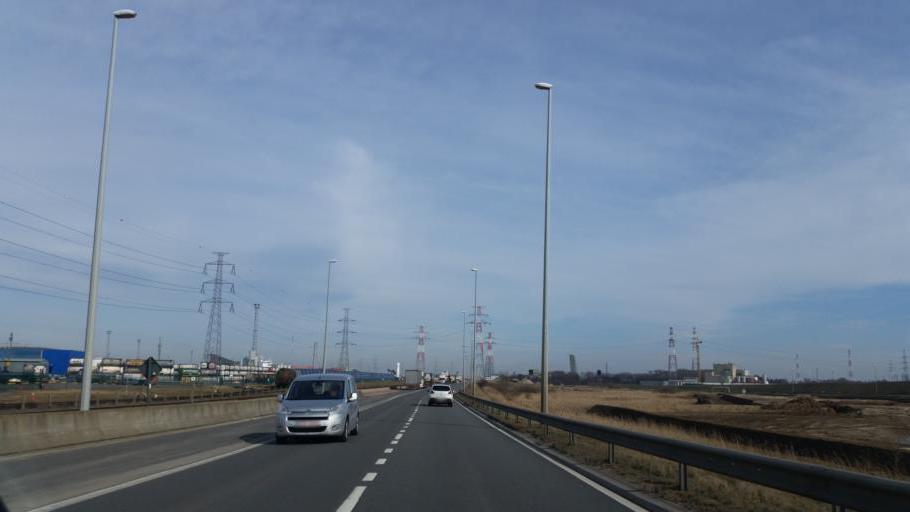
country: BE
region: Flanders
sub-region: Provincie Oost-Vlaanderen
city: Beveren
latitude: 51.2545
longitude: 4.2580
